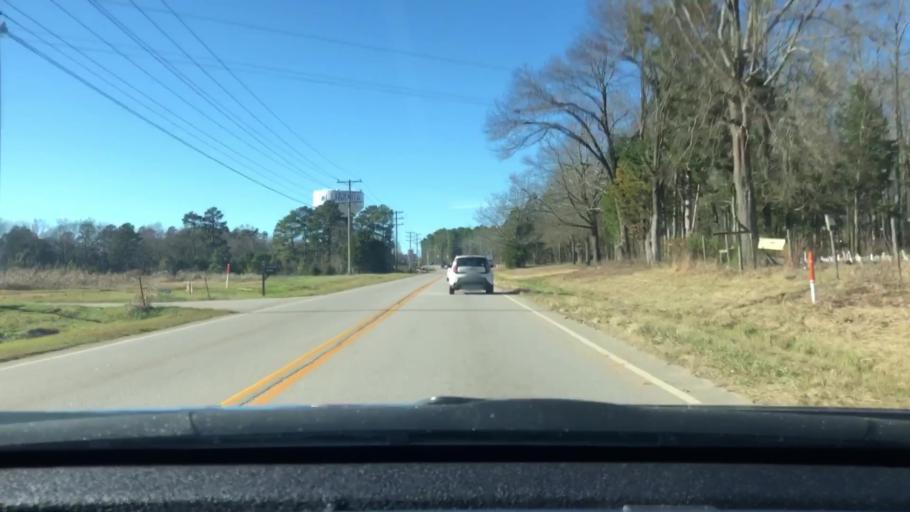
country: US
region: South Carolina
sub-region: Lexington County
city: Irmo
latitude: 34.1171
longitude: -81.2014
